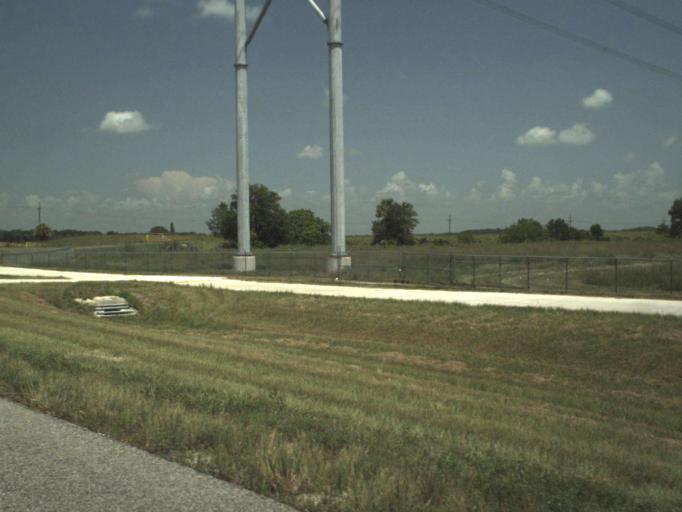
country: US
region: Florida
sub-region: Saint Lucie County
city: Fort Pierce South
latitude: 27.3679
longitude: -80.5451
